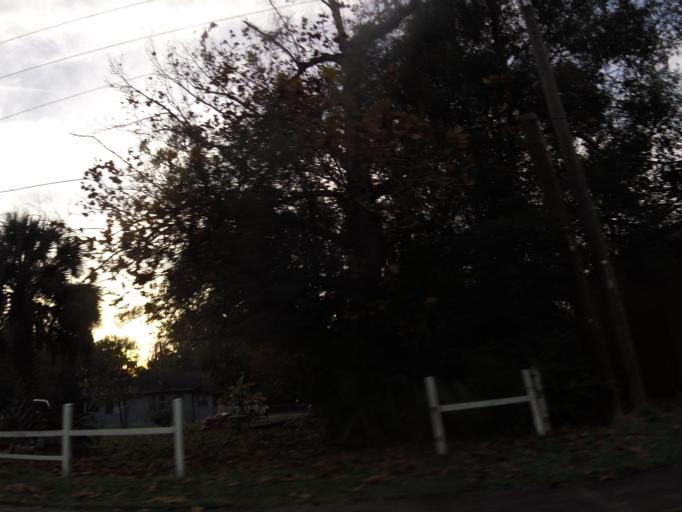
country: US
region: Florida
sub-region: Duval County
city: Jacksonville
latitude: 30.3537
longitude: -81.7186
